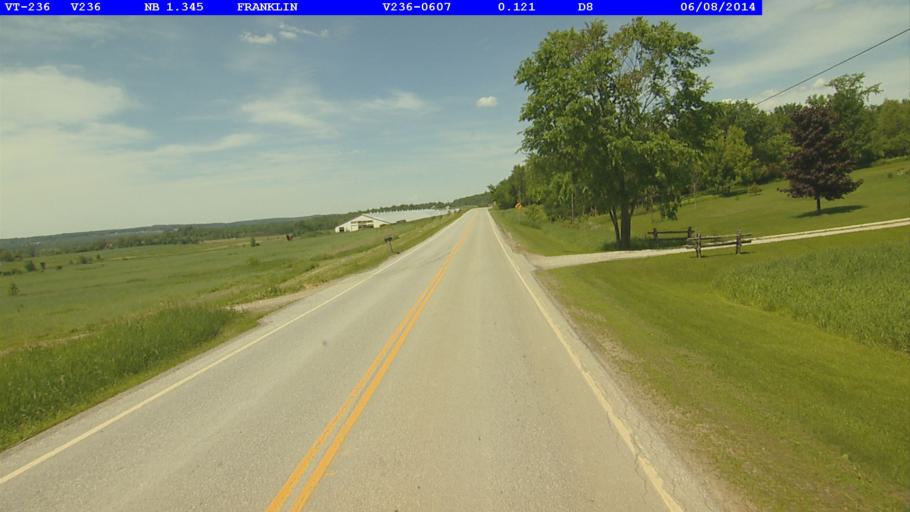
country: US
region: Vermont
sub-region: Franklin County
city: Enosburg Falls
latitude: 44.9302
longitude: -72.8660
